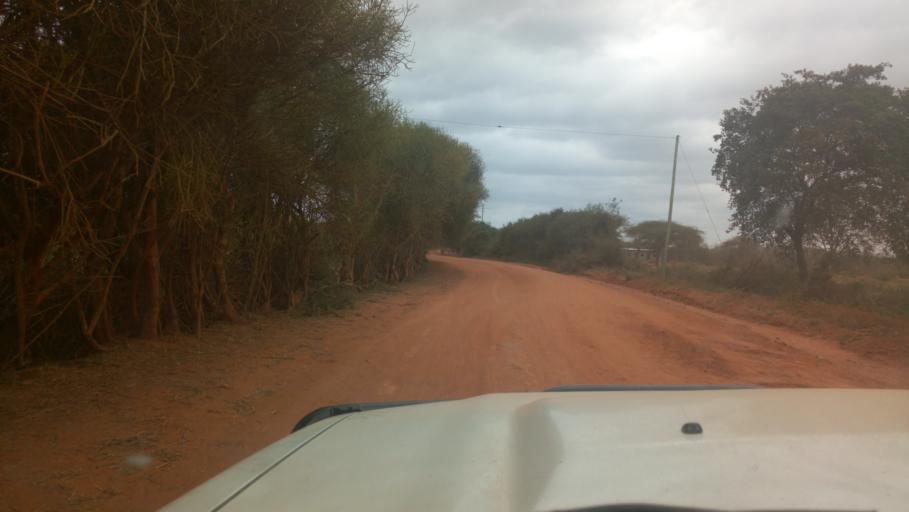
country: KE
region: Makueni
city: Wote
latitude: -1.8958
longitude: 38.0047
